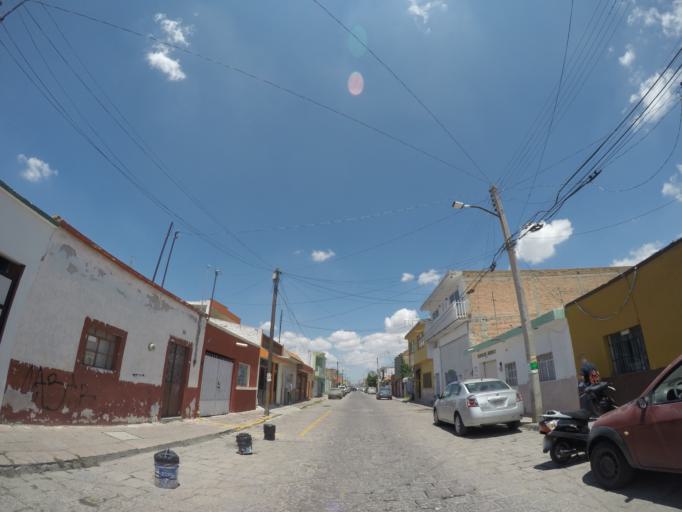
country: MX
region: San Luis Potosi
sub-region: San Luis Potosi
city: San Luis Potosi
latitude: 22.1521
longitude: -100.9607
